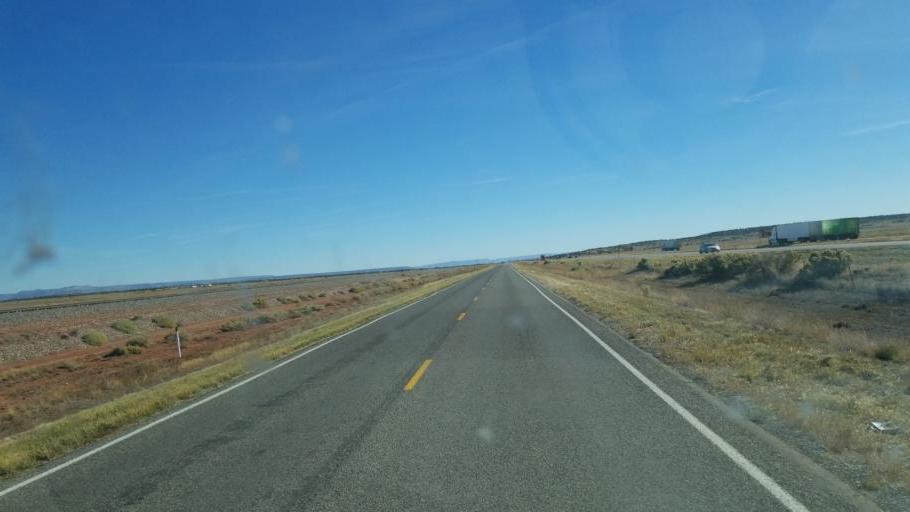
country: US
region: New Mexico
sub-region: Cibola County
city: Milan
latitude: 35.3423
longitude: -108.0066
